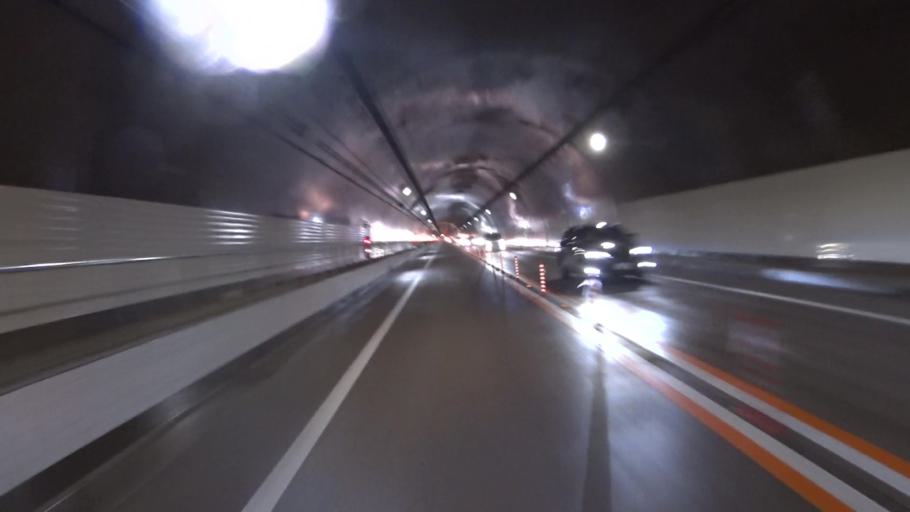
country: JP
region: Kyoto
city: Ayabe
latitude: 35.2505
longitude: 135.3419
